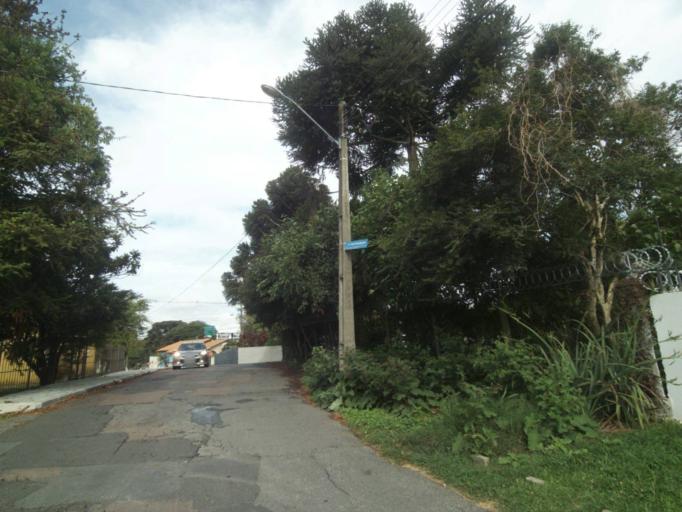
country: BR
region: Parana
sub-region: Curitiba
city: Curitiba
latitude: -25.4389
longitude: -49.3022
